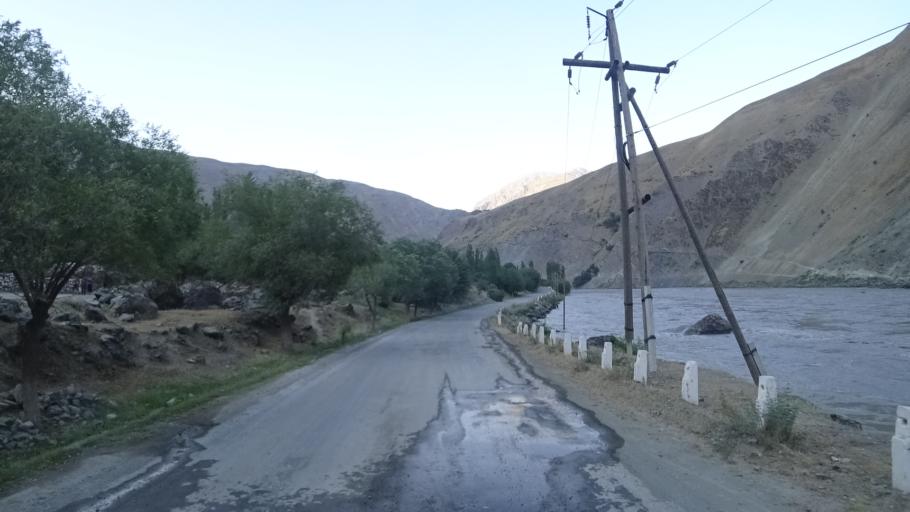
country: TJ
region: Gorno-Badakhshan
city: Qalaikhumb
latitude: 38.4420
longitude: 70.7617
